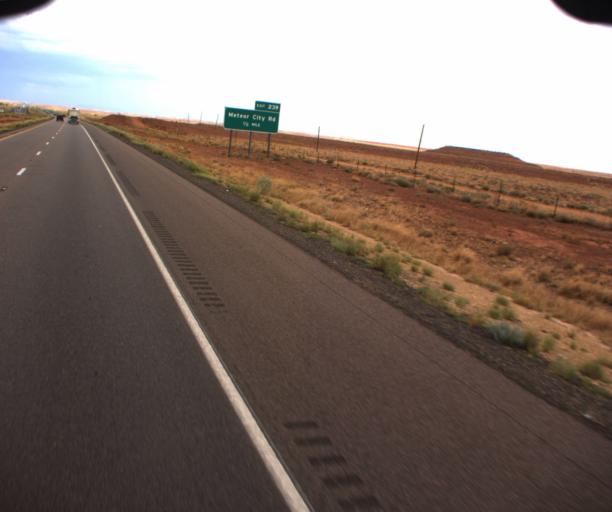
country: US
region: Arizona
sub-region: Coconino County
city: LeChee
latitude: 35.0921
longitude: -110.9168
